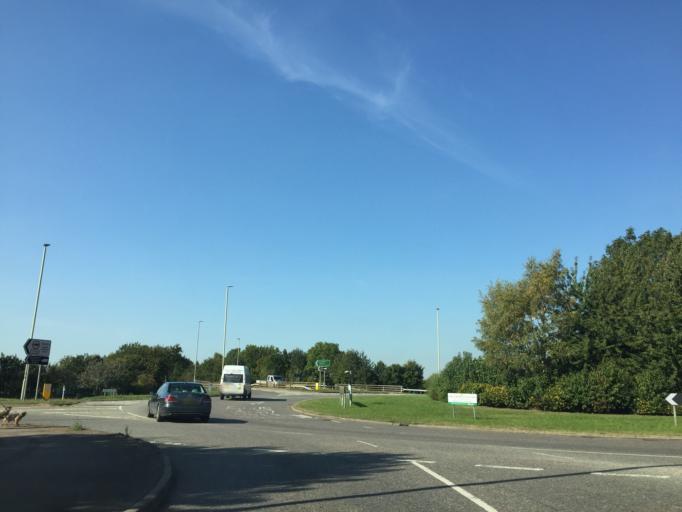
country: GB
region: England
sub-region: Leicestershire
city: Queniborough
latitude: 52.7094
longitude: -1.0505
